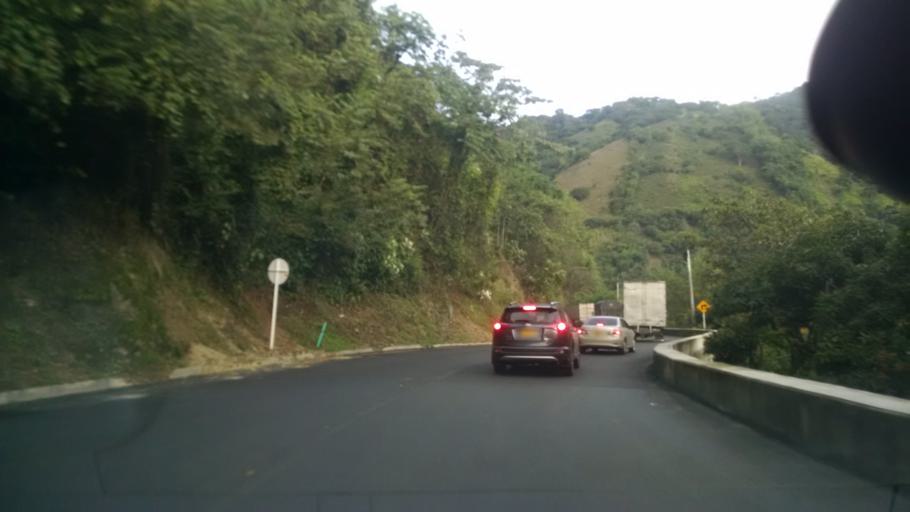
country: CO
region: Antioquia
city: Santa Barbara
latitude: 5.8449
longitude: -75.5791
